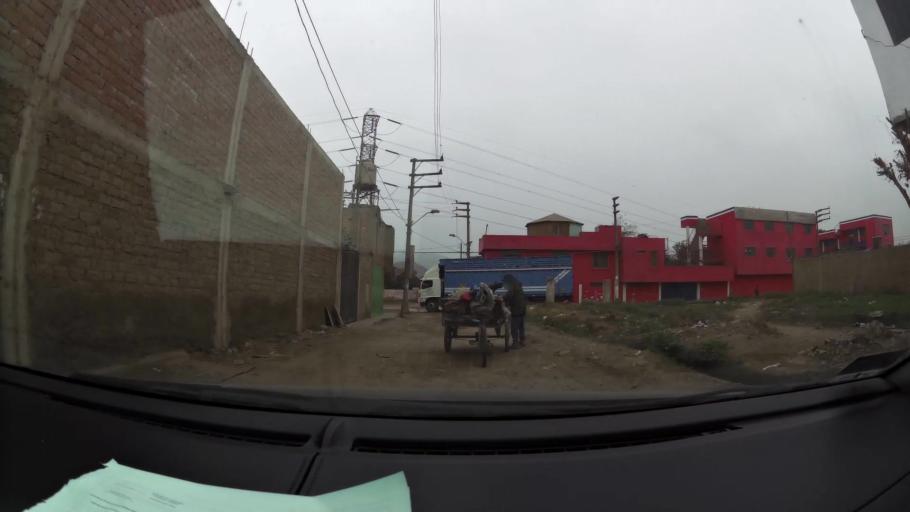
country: PE
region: Lima
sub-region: Lima
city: Urb. Santo Domingo
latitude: -11.8982
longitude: -77.0642
